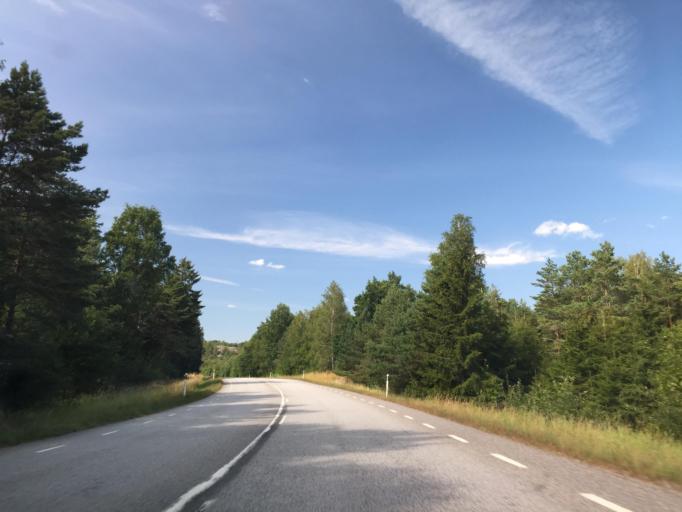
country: SE
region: Vaestra Goetaland
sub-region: Tanums Kommun
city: Tanumshede
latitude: 58.8180
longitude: 11.2627
